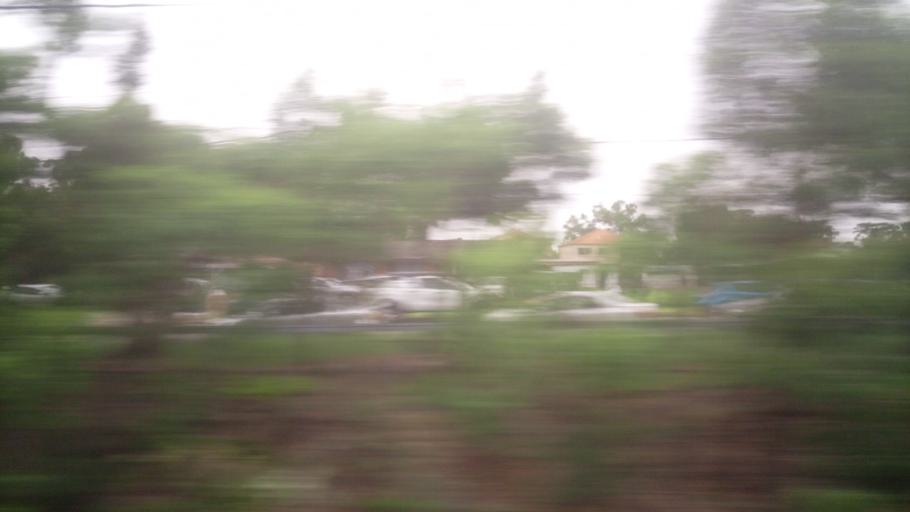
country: AU
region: New South Wales
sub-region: Blacktown
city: Doonside
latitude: -33.7647
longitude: 150.8857
